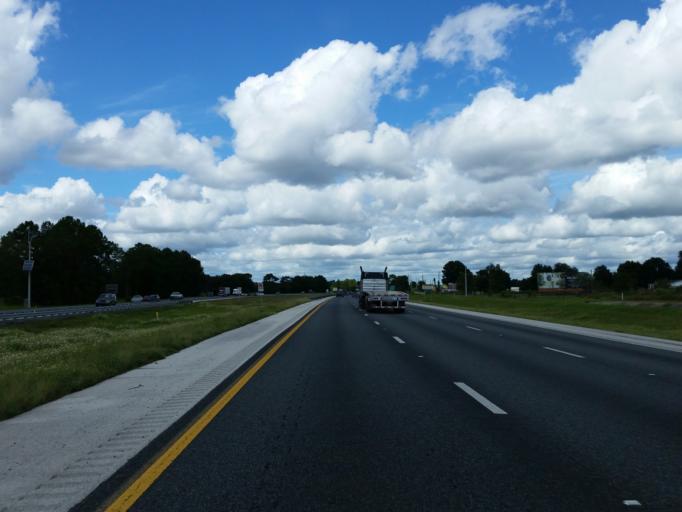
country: US
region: Florida
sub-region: Marion County
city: Belleview
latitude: 29.0034
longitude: -82.1495
